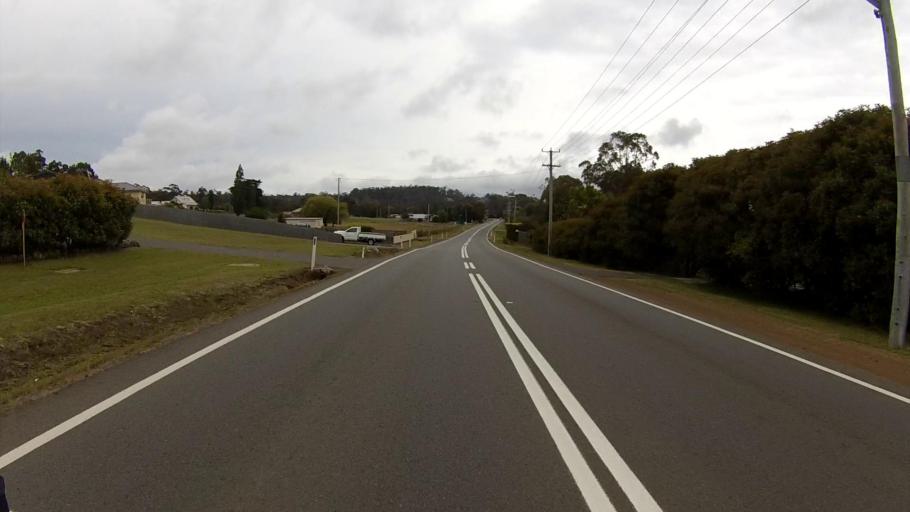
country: AU
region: Tasmania
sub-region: Sorell
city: Sorell
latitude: -42.5520
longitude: 147.8774
